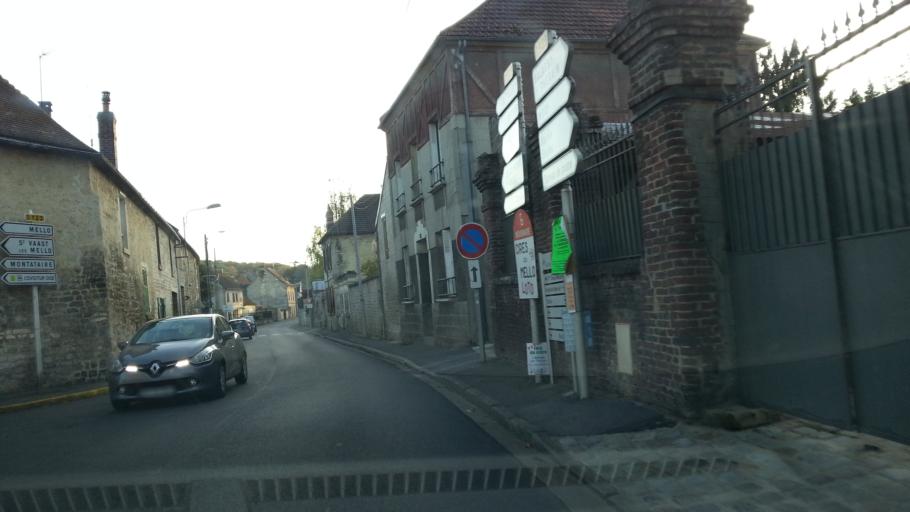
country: FR
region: Picardie
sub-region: Departement de l'Oise
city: Cires-les-Mello
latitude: 49.2731
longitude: 2.3559
